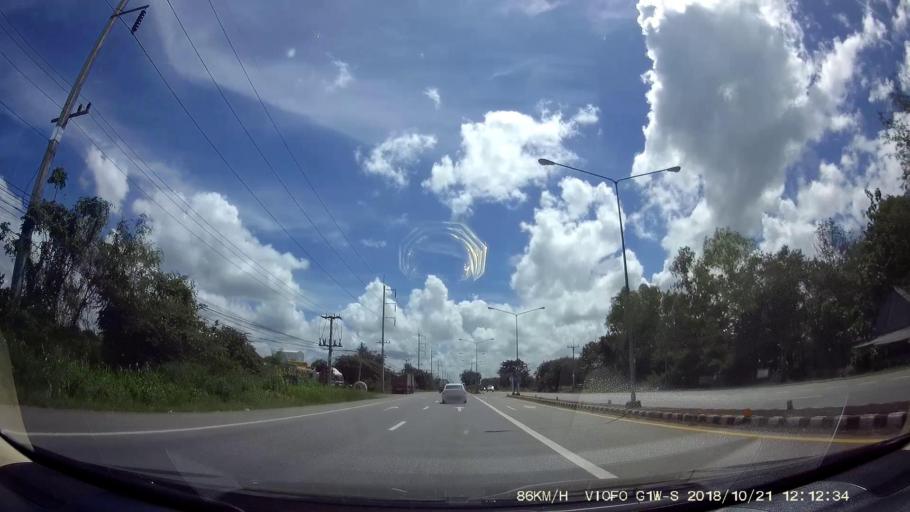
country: TH
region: Chaiyaphum
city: Chatturat
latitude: 15.4053
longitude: 101.8356
